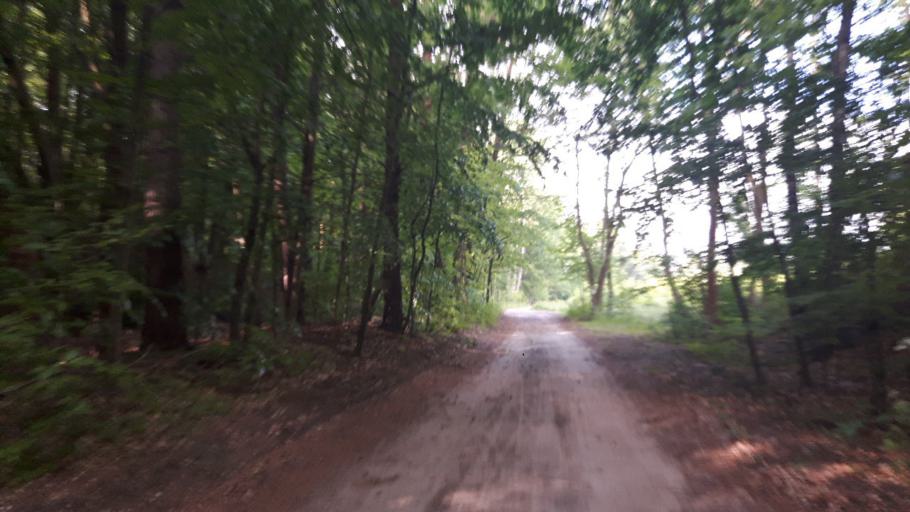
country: PL
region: Pomeranian Voivodeship
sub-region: Slupsk
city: Slupsk
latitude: 54.6105
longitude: 17.0227
